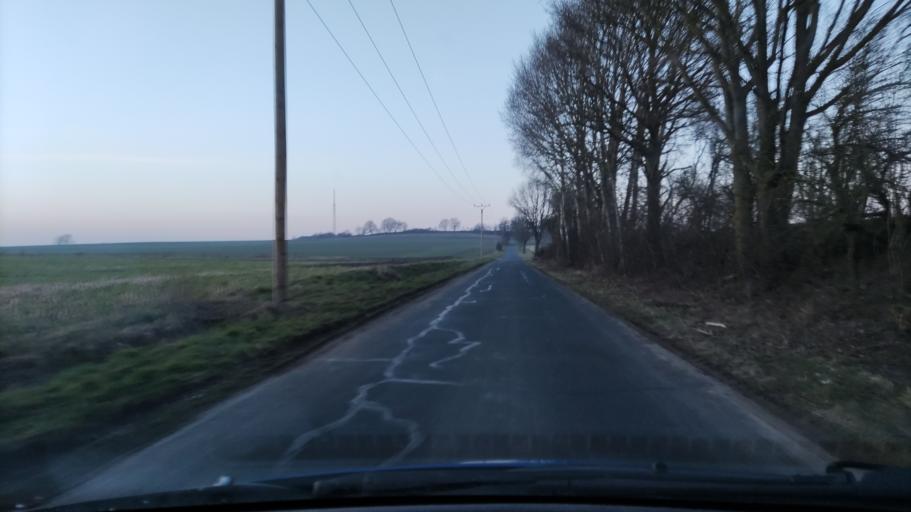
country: DE
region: Lower Saxony
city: Natendorf
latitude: 53.0444
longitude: 10.4796
